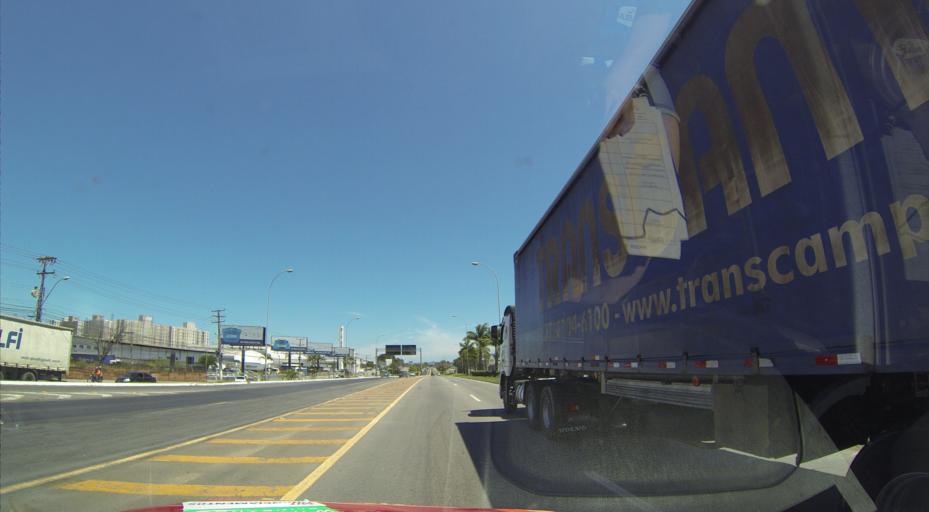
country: BR
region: Espirito Santo
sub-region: Serra
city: Serra
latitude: -20.1965
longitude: -40.2688
